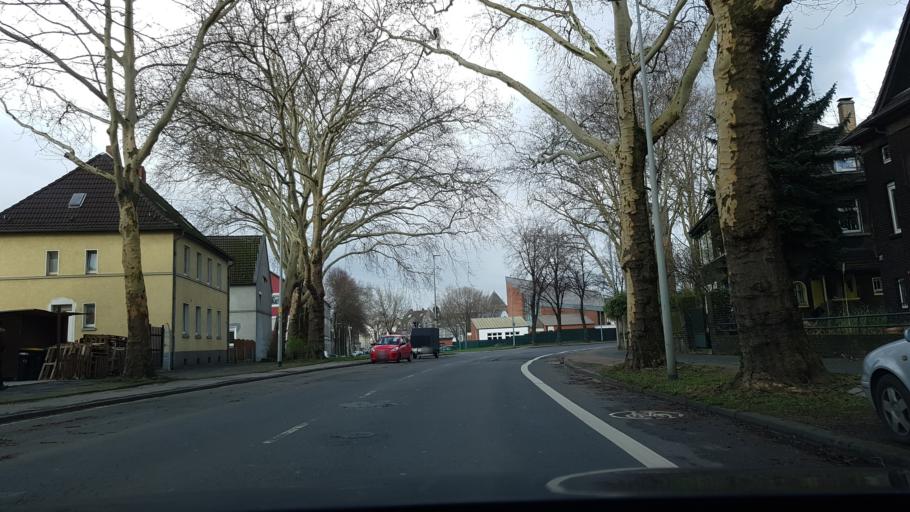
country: DE
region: North Rhine-Westphalia
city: Meiderich
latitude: 51.4724
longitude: 6.7908
